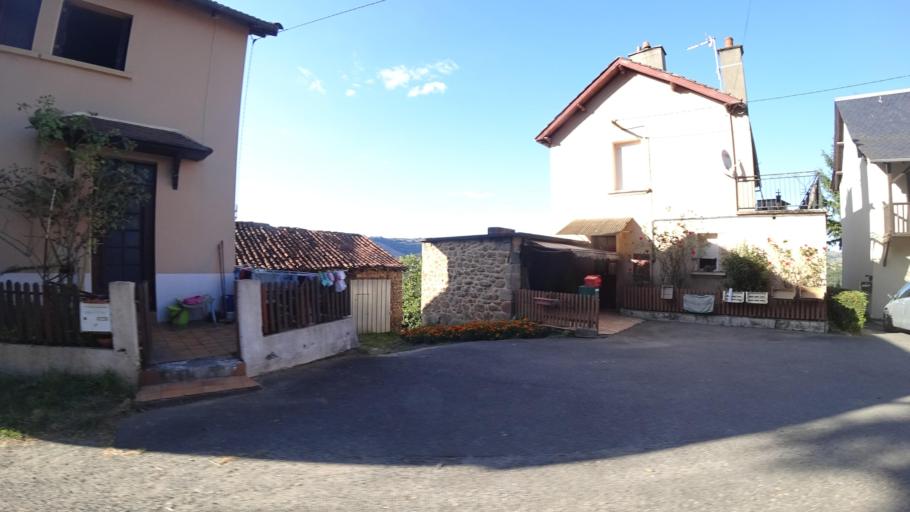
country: FR
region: Midi-Pyrenees
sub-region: Departement de l'Aveyron
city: Firmi
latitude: 44.5290
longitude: 2.3169
